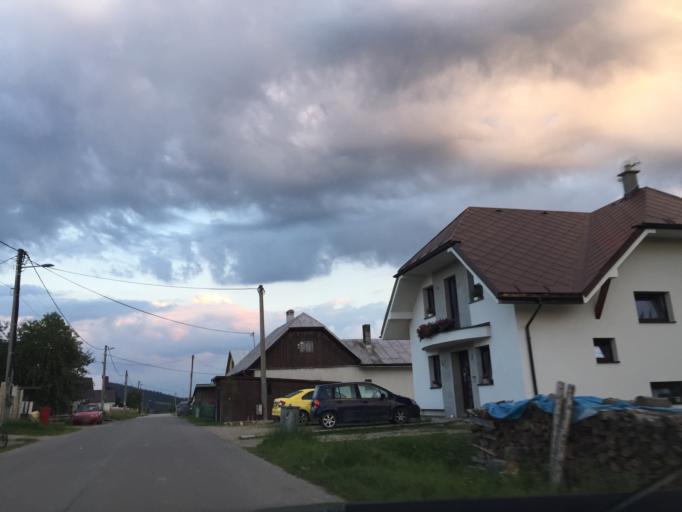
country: PL
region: Silesian Voivodeship
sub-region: Powiat zywiecki
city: Sopotnia Wielka
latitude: 49.4640
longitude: 19.2993
